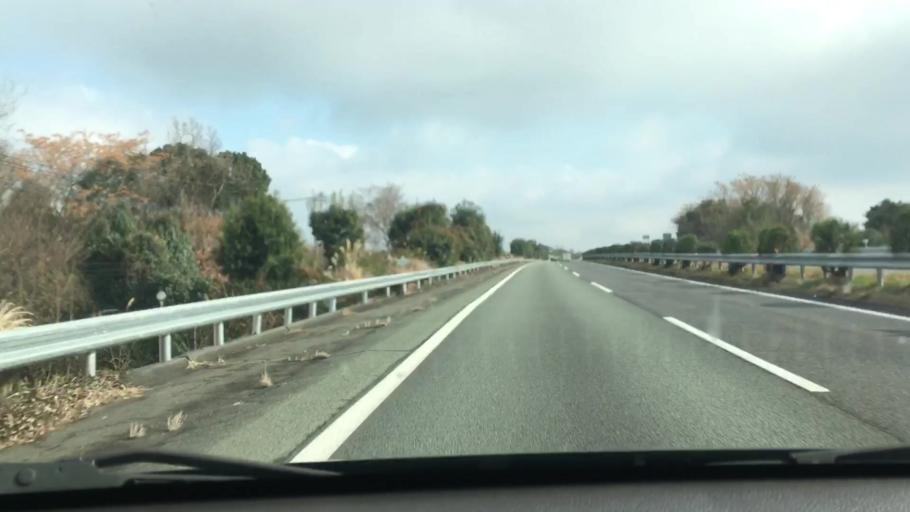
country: JP
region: Kumamoto
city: Kumamoto
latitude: 32.8549
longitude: 130.7578
